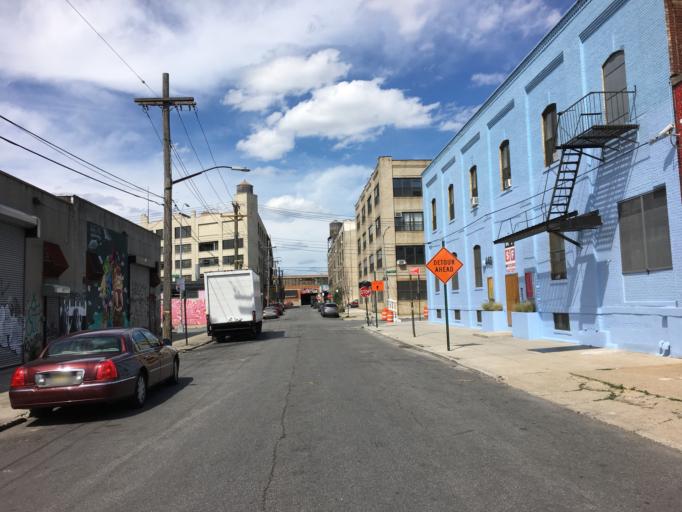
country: US
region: New York
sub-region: Queens County
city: Long Island City
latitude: 40.7077
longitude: -73.9229
